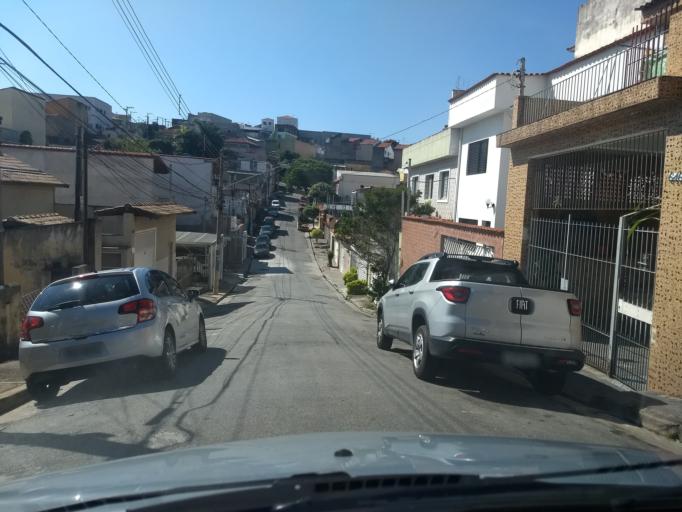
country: BR
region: Sao Paulo
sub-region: Sao Paulo
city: Sao Paulo
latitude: -23.4950
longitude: -46.5956
